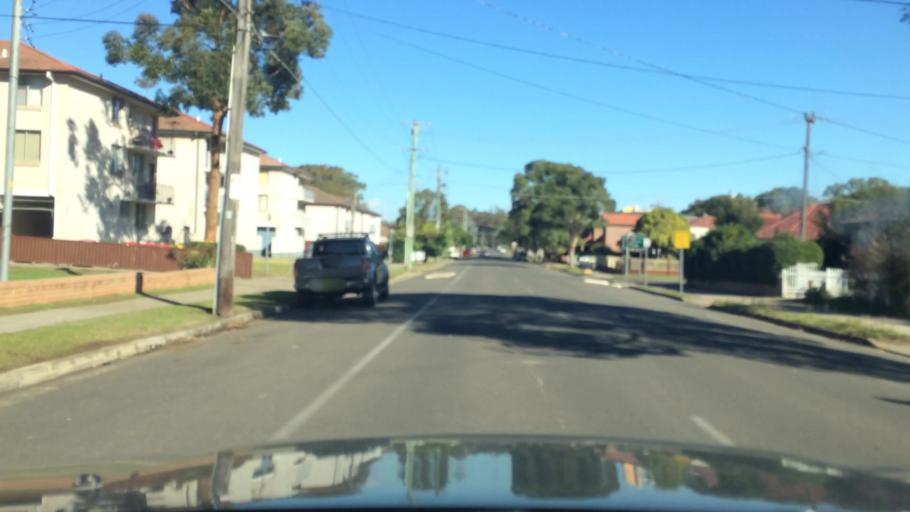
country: AU
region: New South Wales
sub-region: Fairfield
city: Carramar
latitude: -33.8745
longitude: 150.9560
